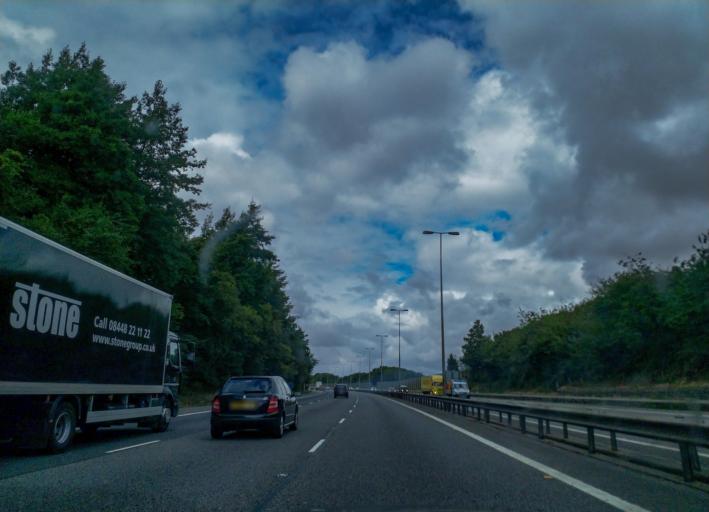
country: GB
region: England
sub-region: Buckinghamshire
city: Stokenchurch
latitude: 51.6545
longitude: -0.8972
